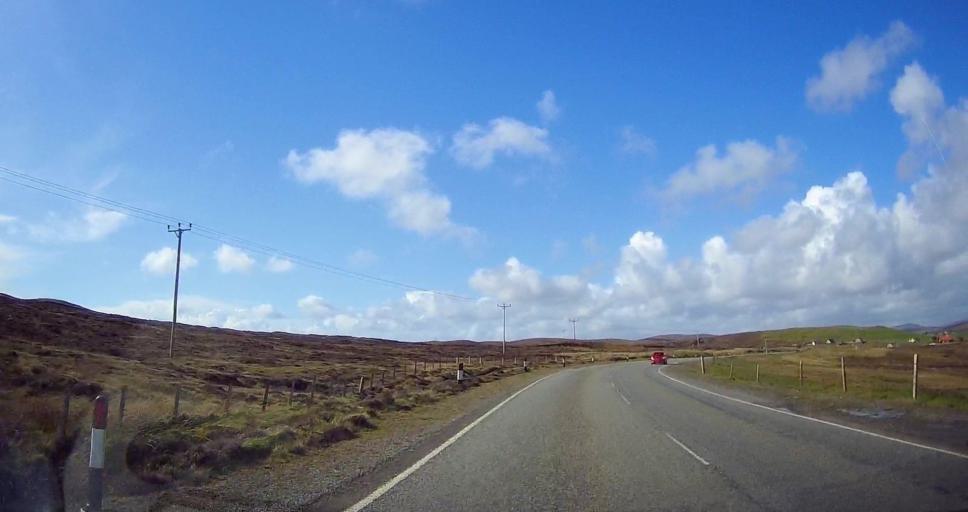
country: GB
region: Scotland
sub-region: Shetland Islands
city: Lerwick
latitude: 60.2282
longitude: -1.2368
